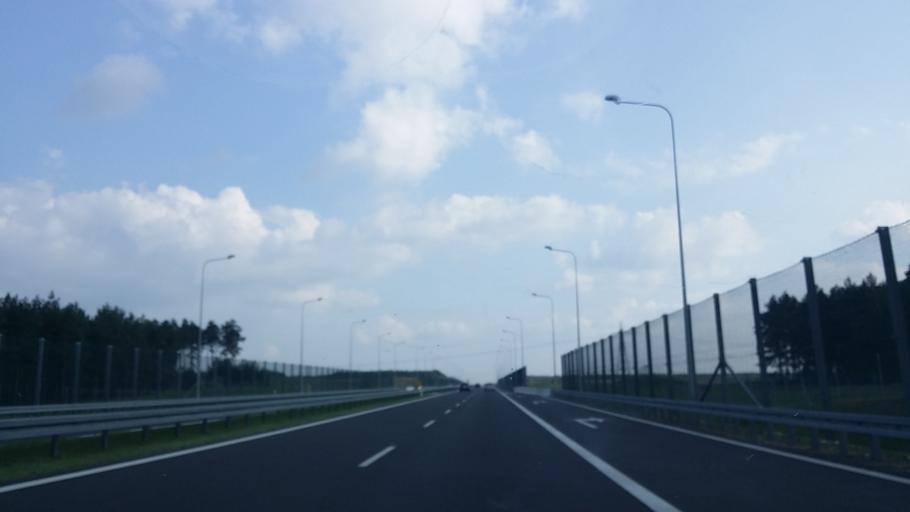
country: PL
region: Lubusz
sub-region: Powiat miedzyrzecki
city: Skwierzyna
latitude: 52.5461
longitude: 15.5406
